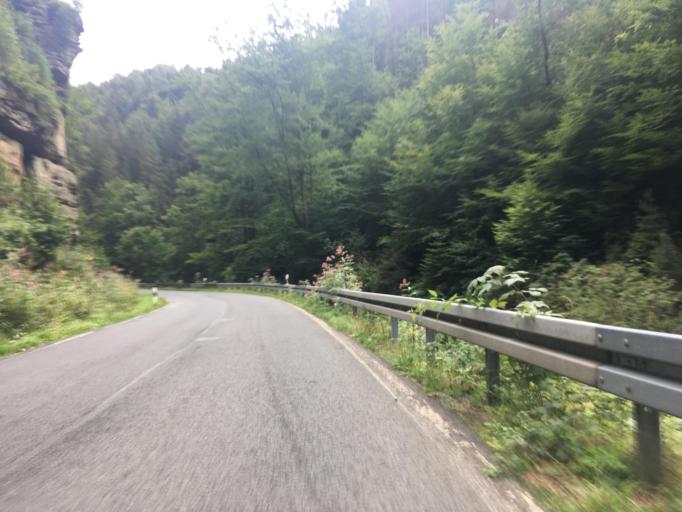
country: DE
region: Saxony
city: Sebnitz
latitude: 50.9285
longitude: 14.2677
